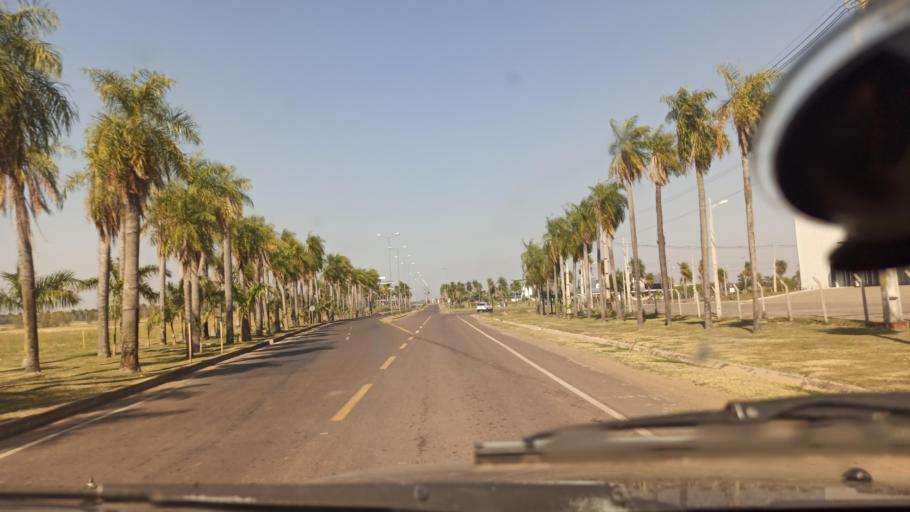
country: PY
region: Central
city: Colonia Mariano Roque Alonso
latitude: -25.1955
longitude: -57.5699
